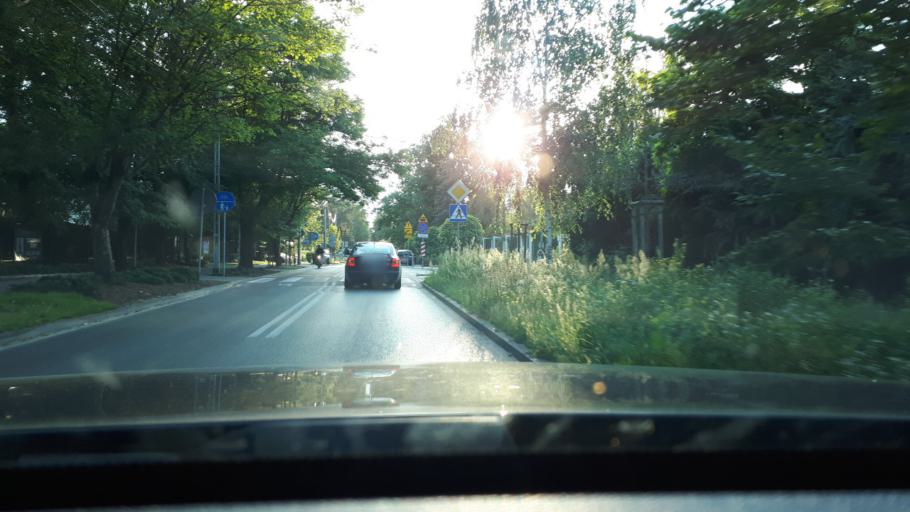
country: PL
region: Masovian Voivodeship
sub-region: Powiat pruszkowski
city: Komorow
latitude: 52.1474
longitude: 20.8138
